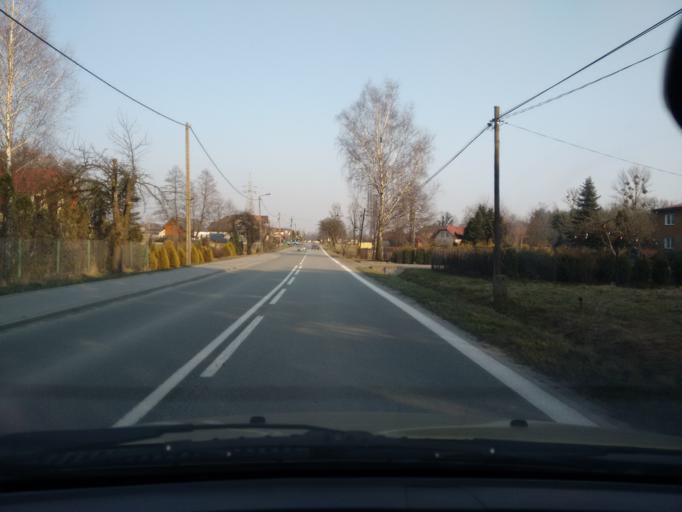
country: PL
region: Silesian Voivodeship
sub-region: Powiat cieszynski
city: Zbytkow
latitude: 49.9165
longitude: 18.7401
